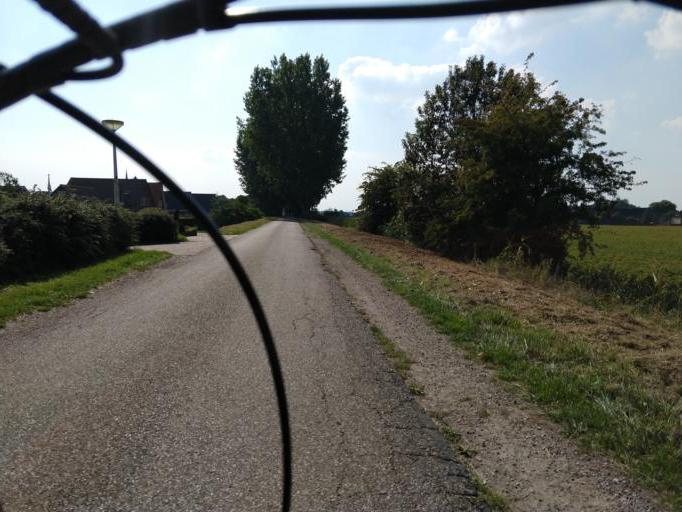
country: NL
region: Zeeland
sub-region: Gemeente Goes
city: Goes
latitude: 51.4373
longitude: 3.8796
